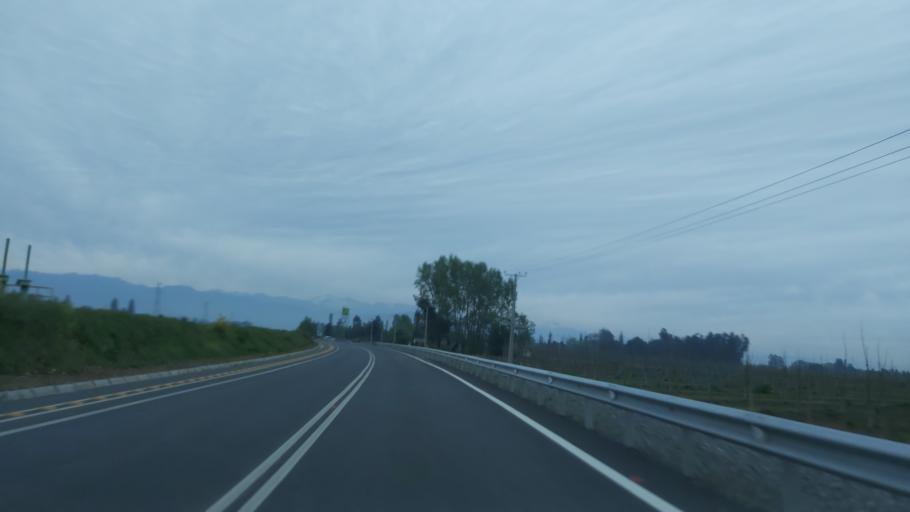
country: CL
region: Maule
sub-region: Provincia de Linares
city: Colbun
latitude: -35.7060
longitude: -71.4837
